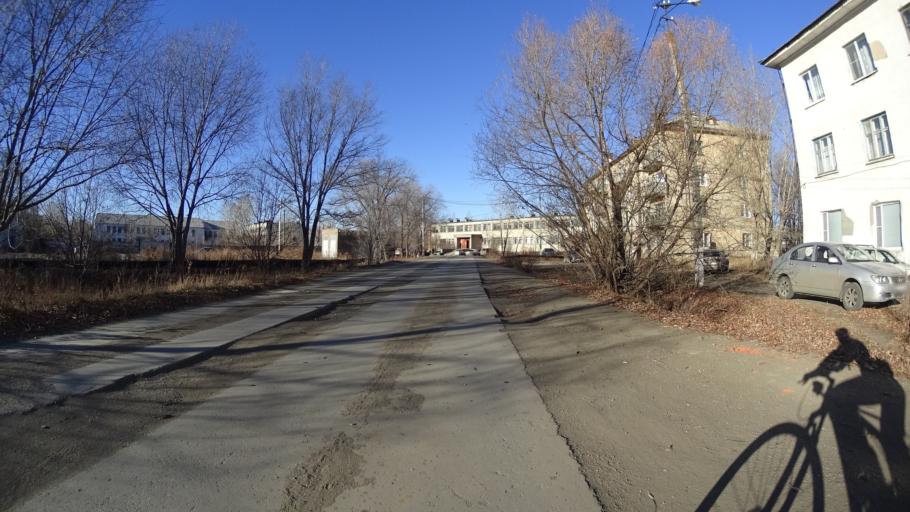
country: RU
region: Chelyabinsk
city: Troitsk
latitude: 54.1088
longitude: 61.5541
